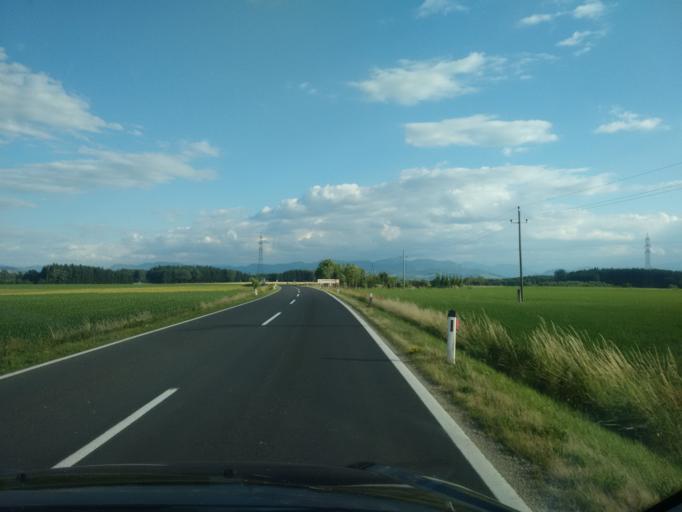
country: AT
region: Upper Austria
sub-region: Politischer Bezirk Steyr-Land
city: Sierning
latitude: 48.0742
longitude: 14.3199
